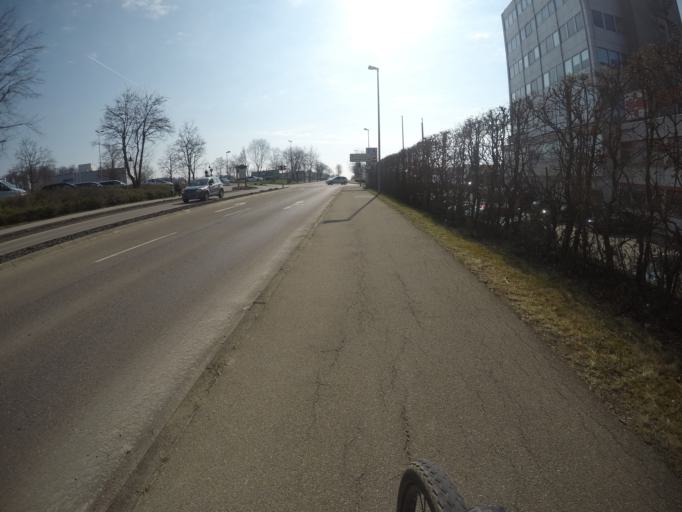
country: DE
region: Baden-Wuerttemberg
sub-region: Regierungsbezirk Stuttgart
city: Wolfschlugen
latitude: 48.6501
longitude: 9.2990
